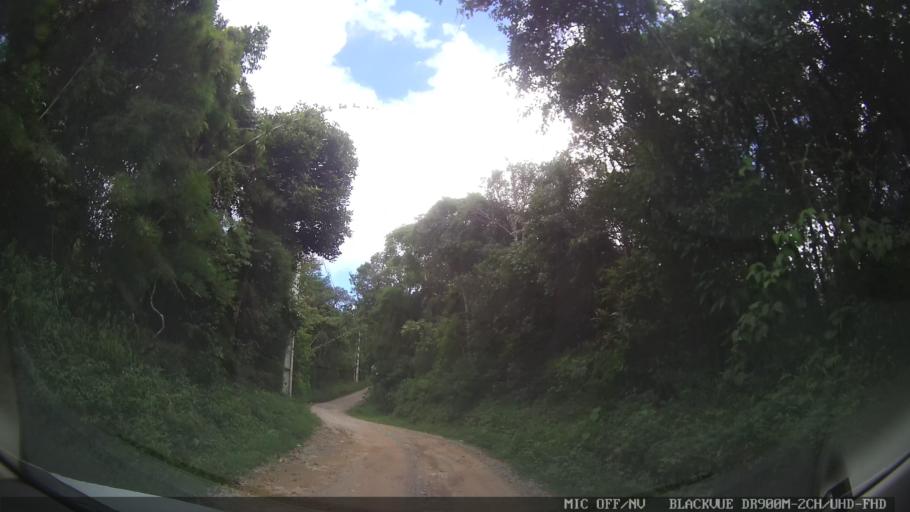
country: BR
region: Minas Gerais
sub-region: Extrema
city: Extrema
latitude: -22.8884
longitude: -46.3166
